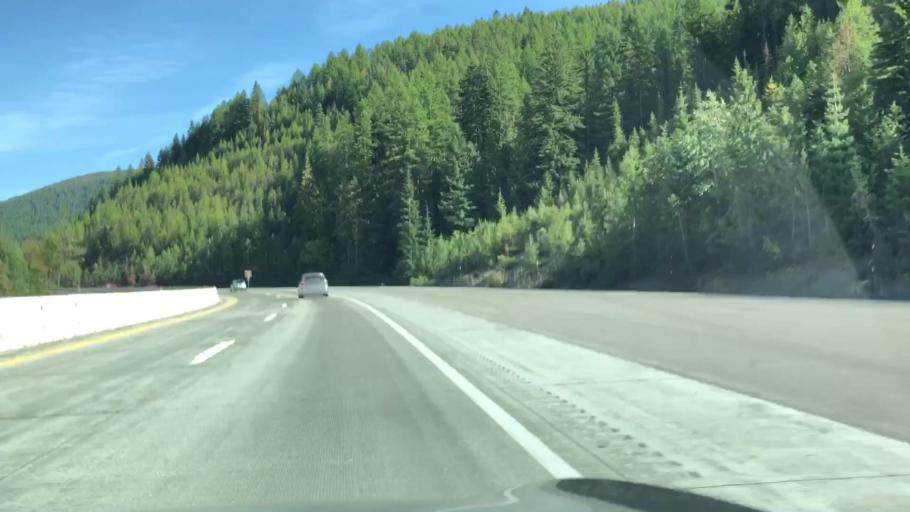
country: US
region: Idaho
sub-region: Shoshone County
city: Wallace
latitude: 47.4636
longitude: -115.7454
